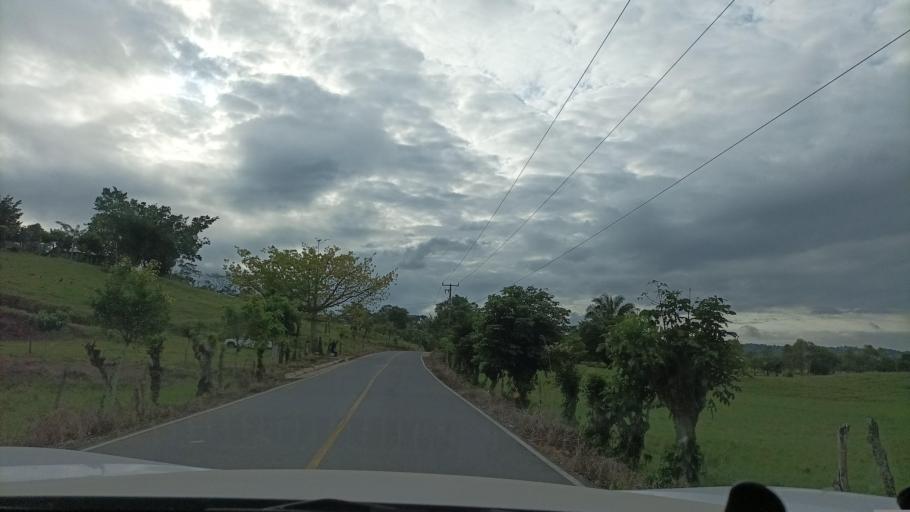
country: MX
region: Veracruz
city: Hidalgotitlan
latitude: 17.7432
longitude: -94.4913
